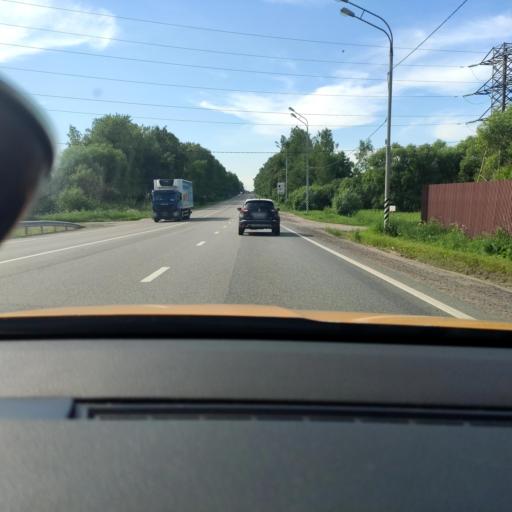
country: RU
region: Moskovskaya
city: Mikhnevo
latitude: 55.1698
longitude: 37.9101
